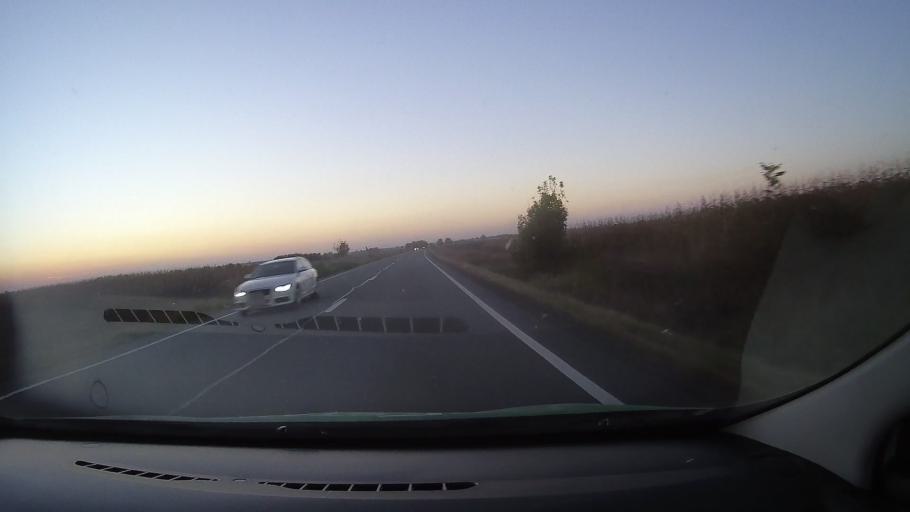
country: RO
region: Bihor
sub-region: Comuna Tarcea
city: Tarcea
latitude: 47.4373
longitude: 22.1982
